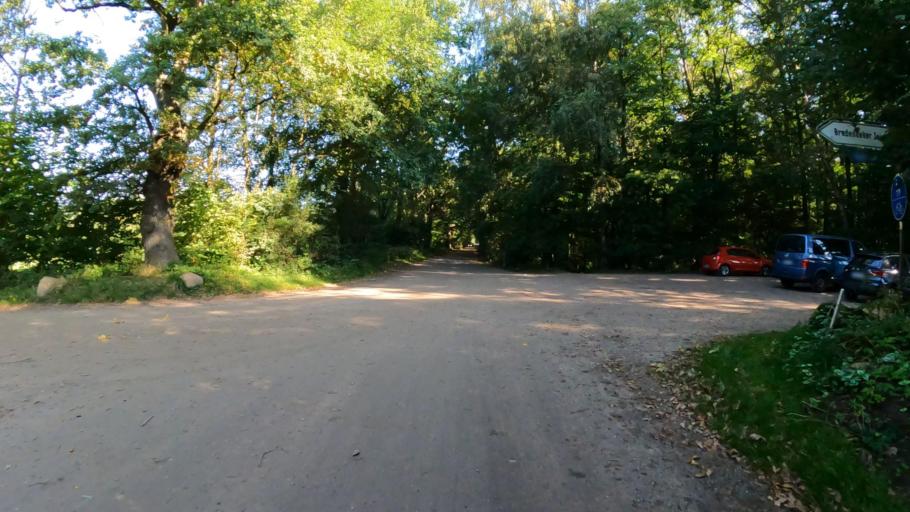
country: DE
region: Schleswig-Holstein
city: Ahrensburg
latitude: 53.6684
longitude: 10.2032
